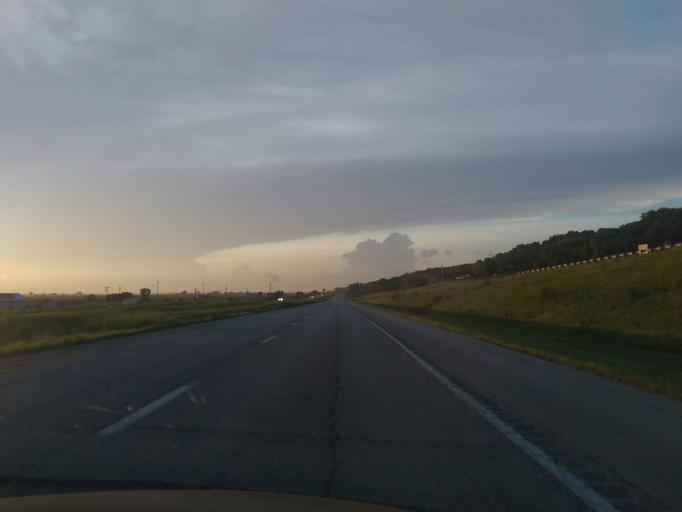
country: US
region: Missouri
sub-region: Atchison County
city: Rock Port
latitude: 40.4086
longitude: -95.5560
